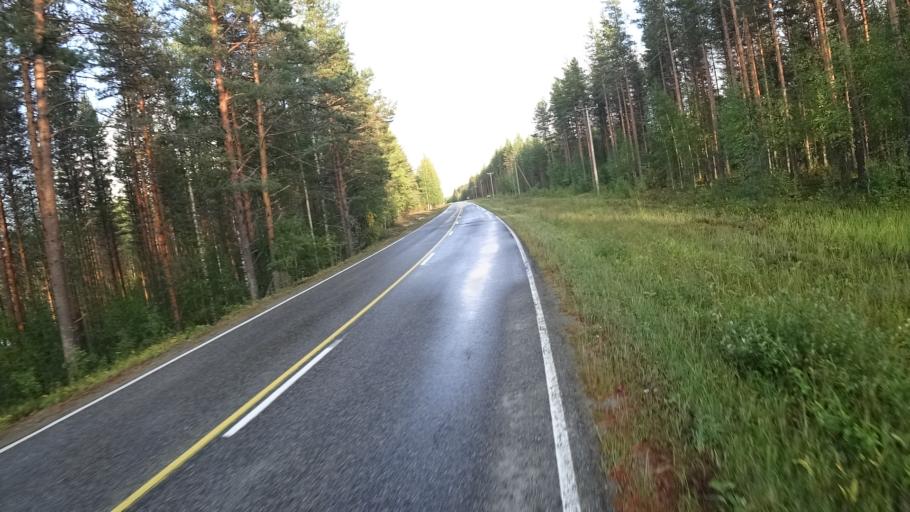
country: FI
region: North Karelia
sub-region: Joensuu
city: Ilomantsi
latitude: 62.6279
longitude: 31.0972
